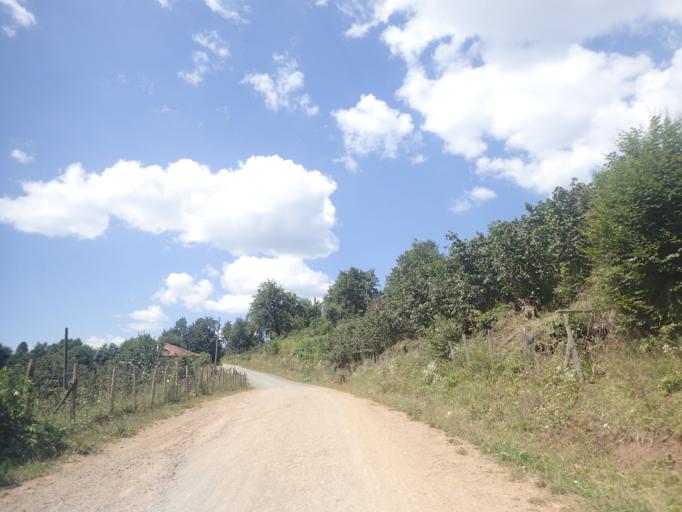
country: TR
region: Ordu
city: Aybasti
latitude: 40.6945
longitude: 37.3246
